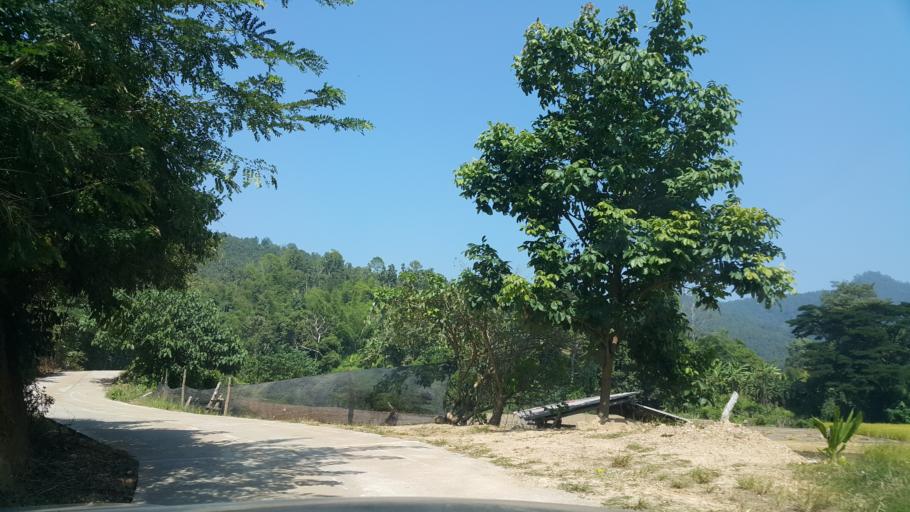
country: TH
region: Chiang Mai
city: Samoeng
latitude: 18.9203
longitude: 98.6097
